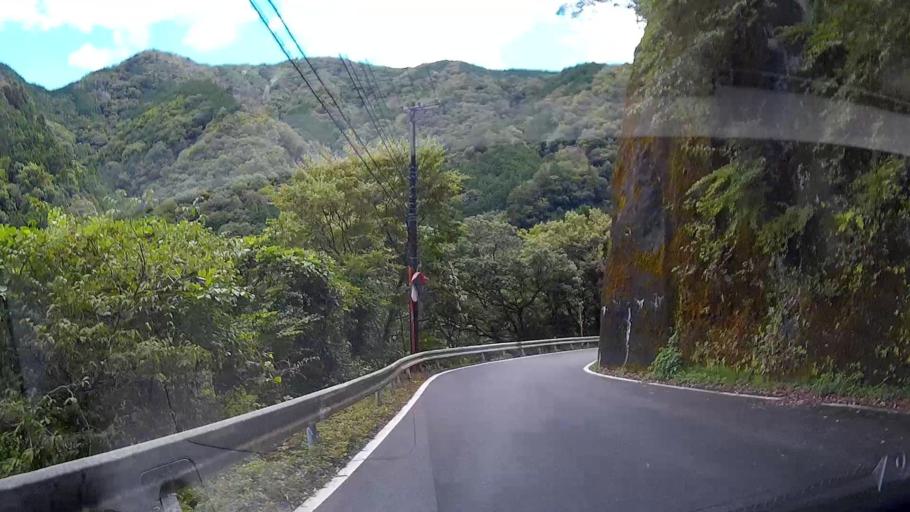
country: JP
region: Shizuoka
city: Shizuoka-shi
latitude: 35.2304
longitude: 138.3464
